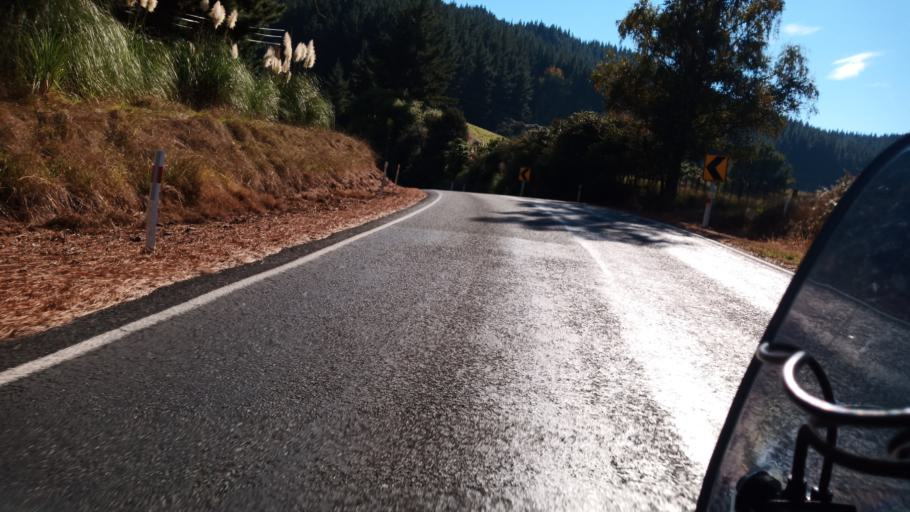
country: NZ
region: Hawke's Bay
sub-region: Wairoa District
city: Wairoa
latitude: -38.9276
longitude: 177.2742
